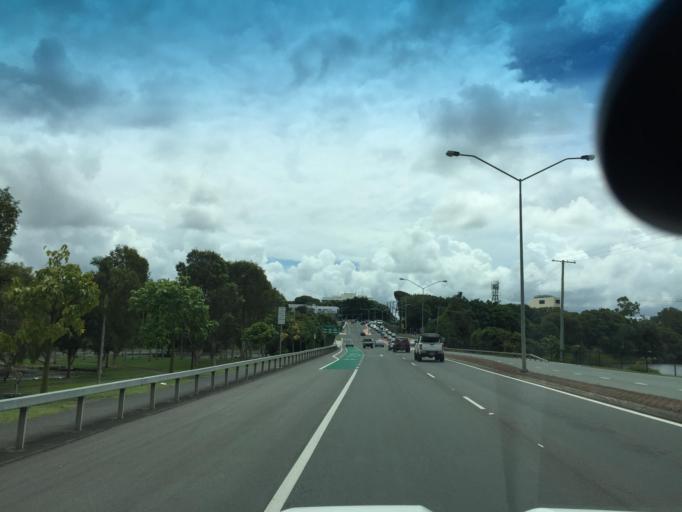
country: AU
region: Queensland
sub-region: Moreton Bay
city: Caboolture
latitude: -27.0884
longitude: 152.9507
